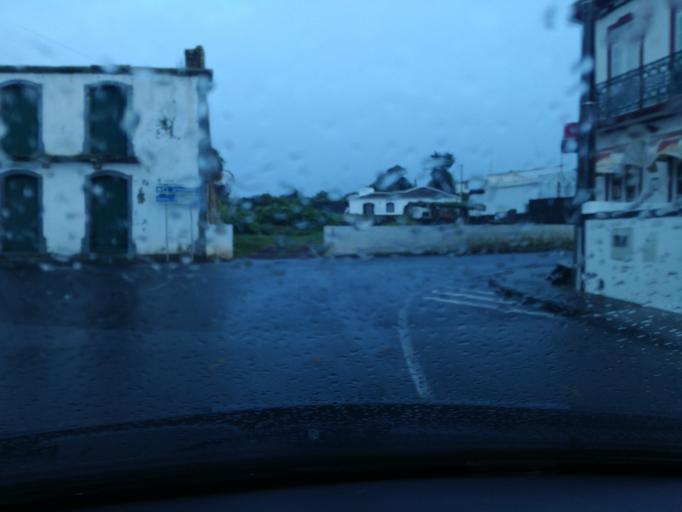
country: PT
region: Azores
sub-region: Praia da Vitoria
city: Praia da Vitoria
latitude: 38.7065
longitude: -27.0586
